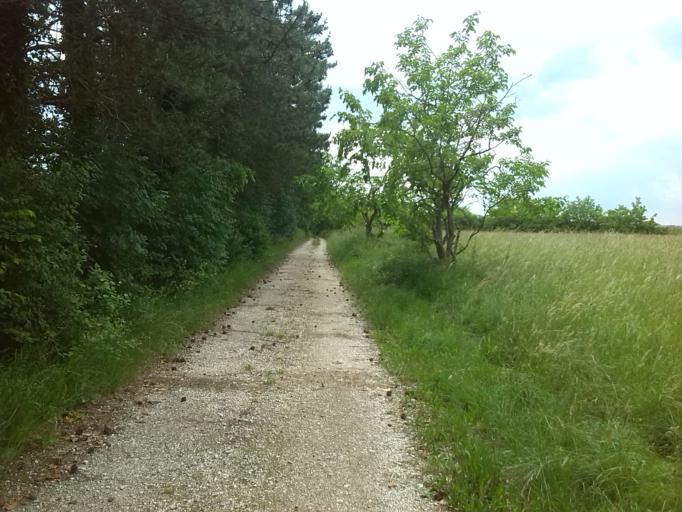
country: IT
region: Friuli Venezia Giulia
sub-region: Provincia di Udine
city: Cividale del Friuli
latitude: 46.0956
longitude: 13.4475
